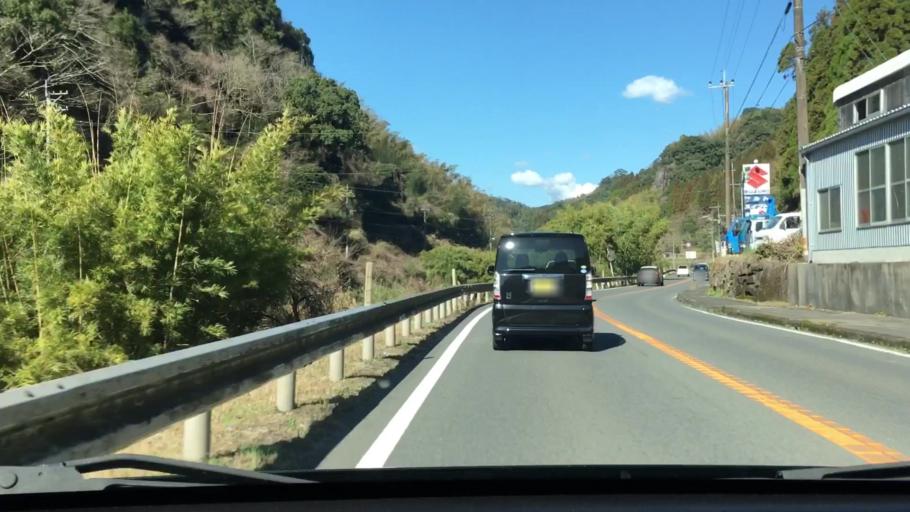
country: JP
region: Kagoshima
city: Kagoshima-shi
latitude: 31.6454
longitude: 130.5143
